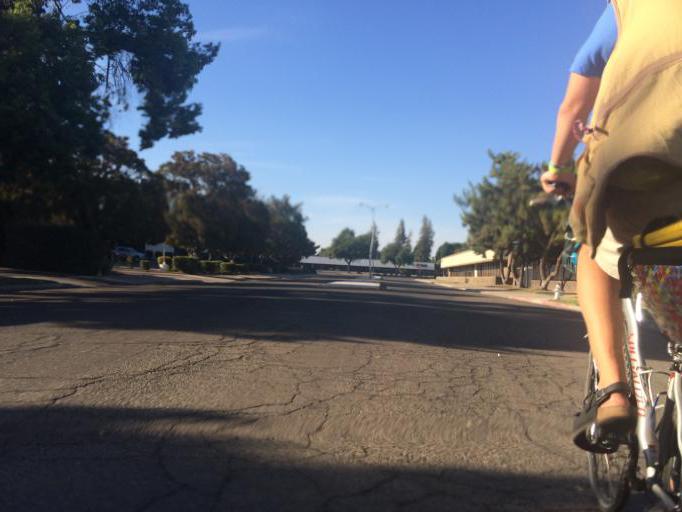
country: US
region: California
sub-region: Fresno County
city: Clovis
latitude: 36.8072
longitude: -119.7598
